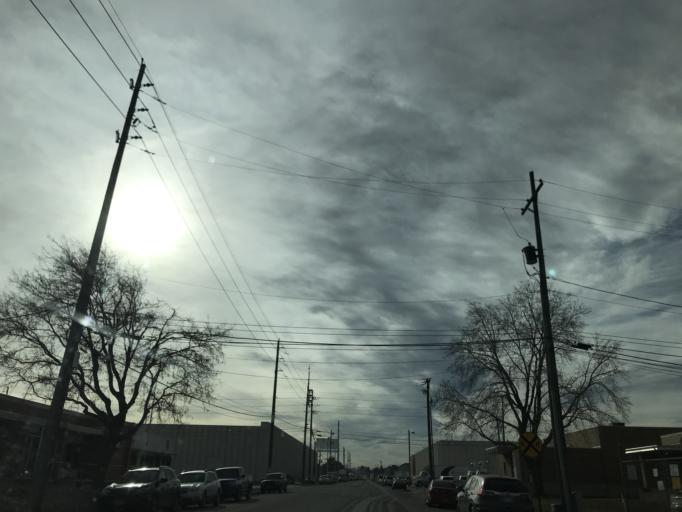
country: US
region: Colorado
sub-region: Adams County
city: Commerce City
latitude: 39.7778
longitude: -104.9083
